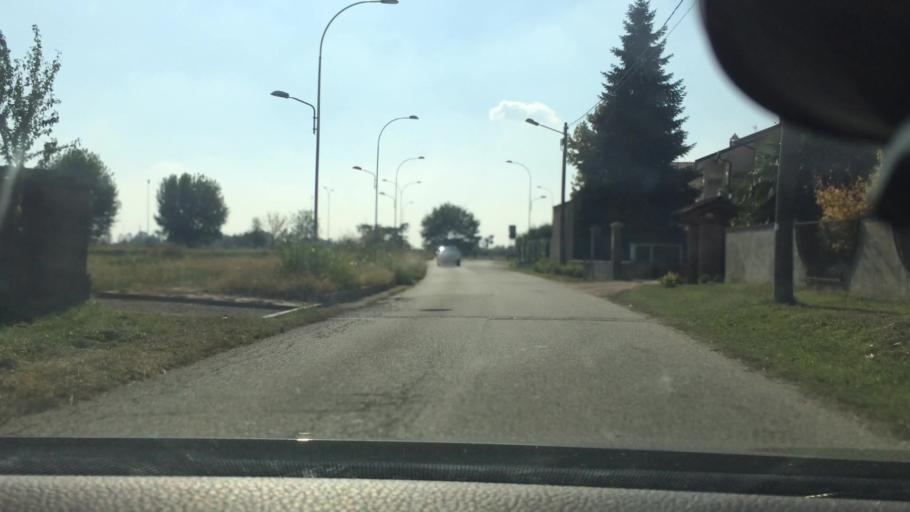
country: IT
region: Lombardy
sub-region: Citta metropolitana di Milano
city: Mesero
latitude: 45.4985
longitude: 8.8470
